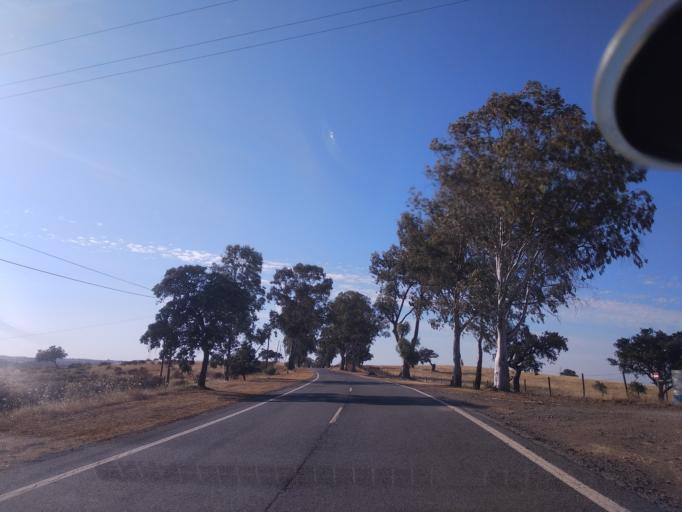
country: PT
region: Beja
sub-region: Almodovar
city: Almodovar
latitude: 37.4526
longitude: -7.9966
